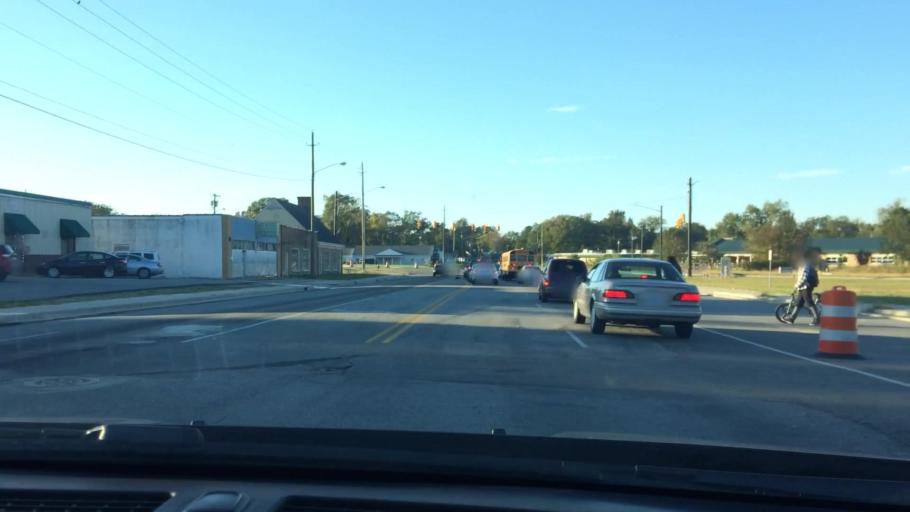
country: US
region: North Carolina
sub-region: Pitt County
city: Greenville
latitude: 35.6072
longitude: -77.3848
